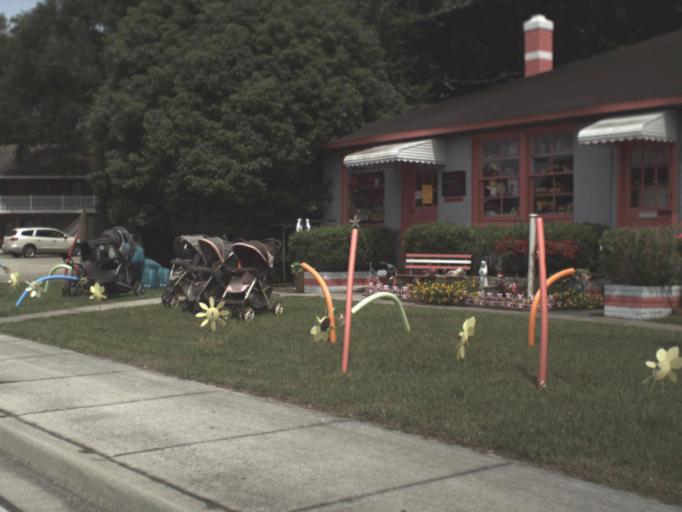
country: US
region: Florida
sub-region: Duval County
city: Jacksonville
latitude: 30.2766
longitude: -81.7295
